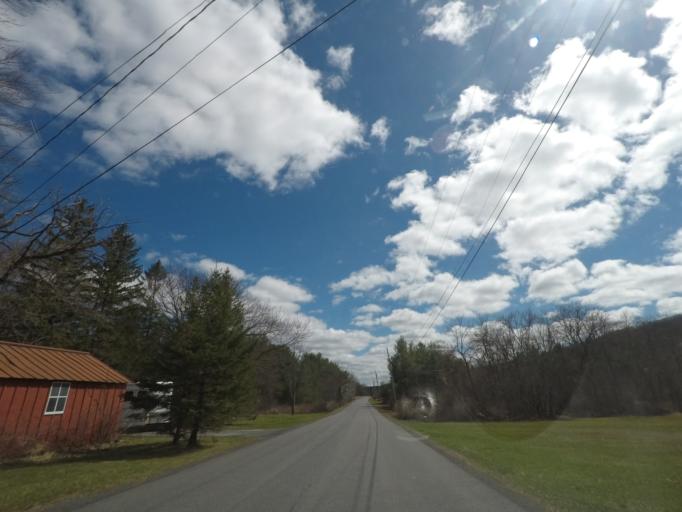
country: US
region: New York
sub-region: Albany County
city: Voorheesville
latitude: 42.6139
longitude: -73.9595
